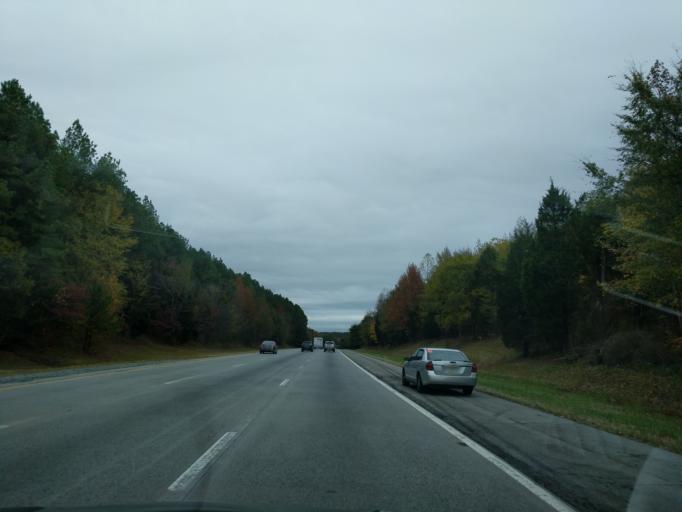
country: US
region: North Carolina
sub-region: Davidson County
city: Lexington
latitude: 35.8223
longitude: -80.1693
